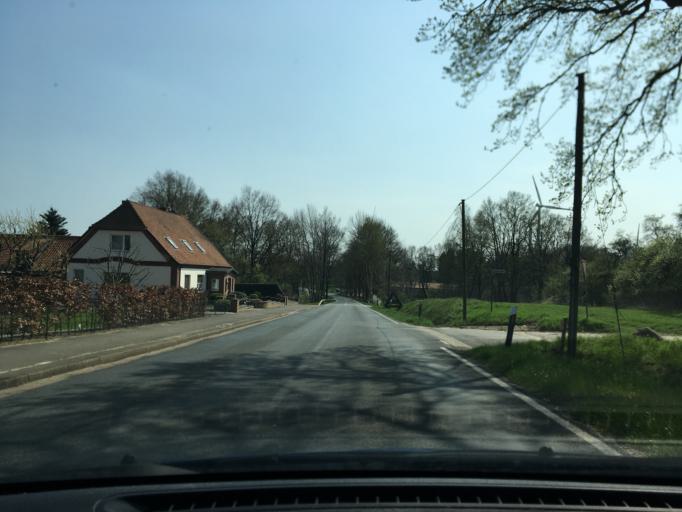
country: DE
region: Lower Saxony
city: Sudergellersen
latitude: 53.2057
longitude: 10.3004
